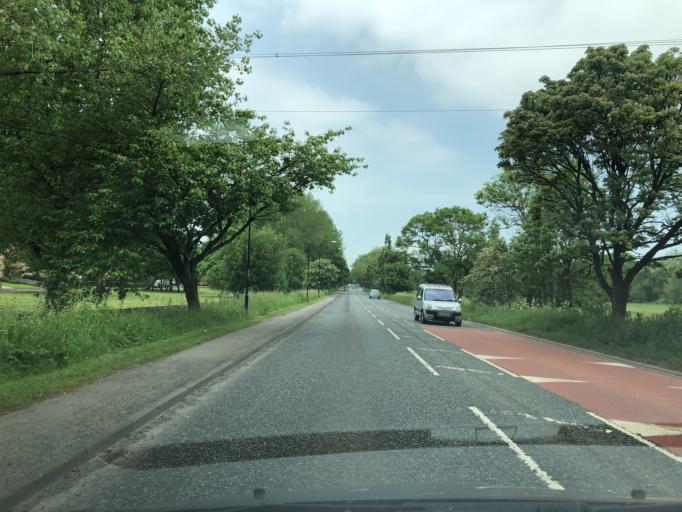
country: GB
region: England
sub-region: North Yorkshire
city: Harrogate
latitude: 54.0070
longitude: -1.5562
